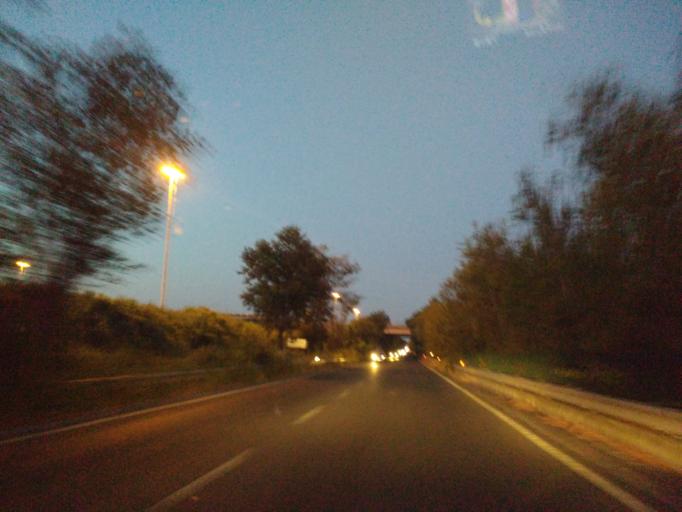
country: IT
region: Latium
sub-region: Citta metropolitana di Roma Capitale
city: Acilia-Castel Fusano-Ostia Antica
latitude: 41.7738
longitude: 12.3350
